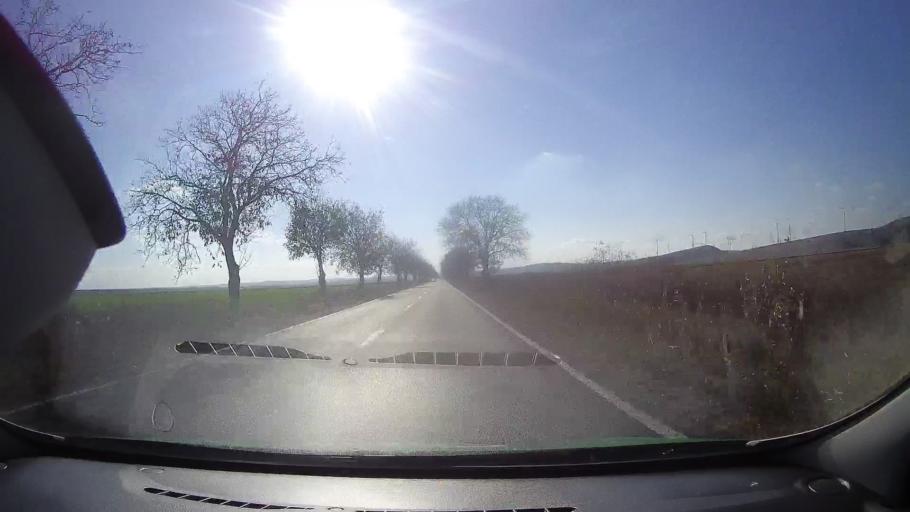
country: RO
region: Tulcea
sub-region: Comuna Ceamurlia de Jos
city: Ceamurlia de Jos
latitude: 44.7932
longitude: 28.6900
